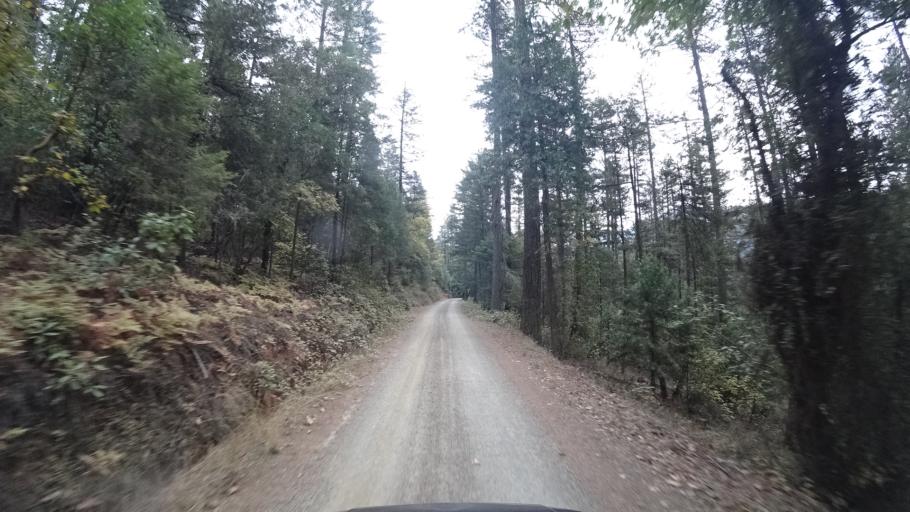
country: US
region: California
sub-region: Siskiyou County
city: Happy Camp
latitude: 41.7829
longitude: -123.3322
